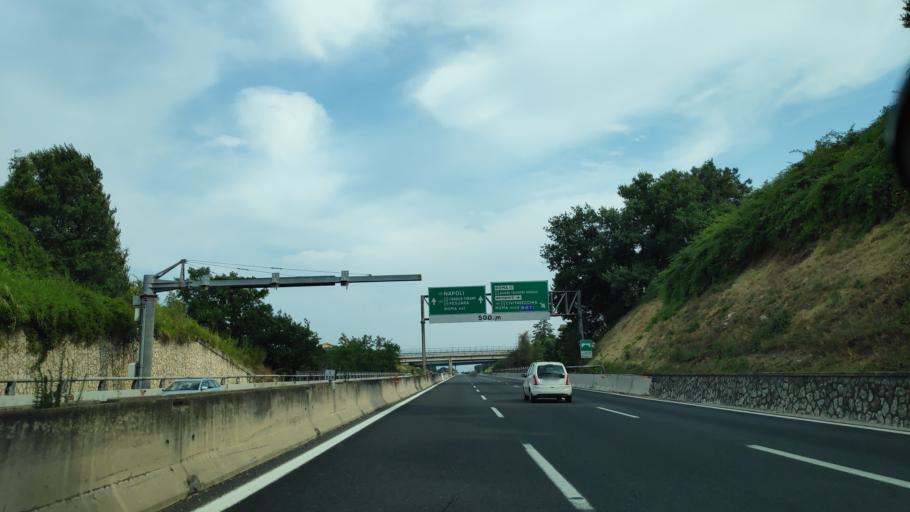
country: IT
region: Latium
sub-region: Citta metropolitana di Roma Capitale
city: Fiano Romano
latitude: 42.1768
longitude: 12.6049
